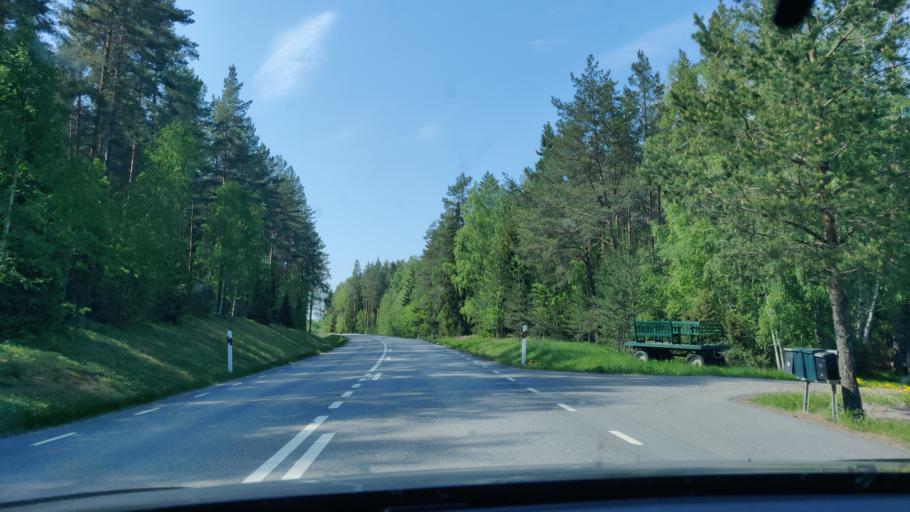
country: SE
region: Uppsala
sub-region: Heby Kommun
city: OEstervala
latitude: 60.1422
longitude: 17.2119
